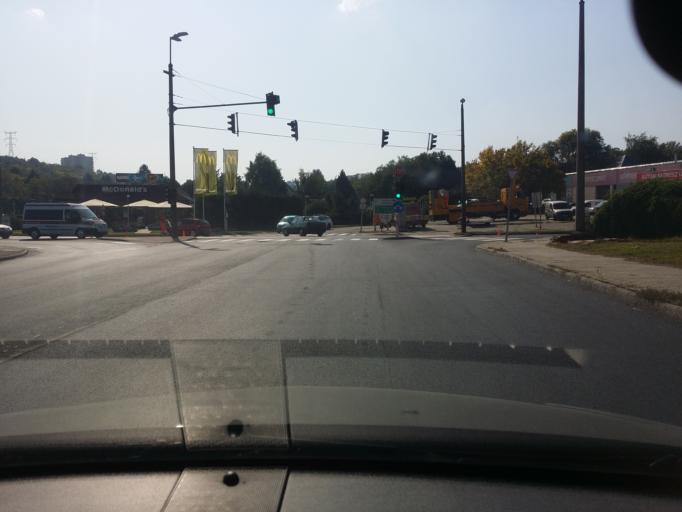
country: HU
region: Fejer
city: dunaujvaros
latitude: 46.9742
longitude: 18.9275
